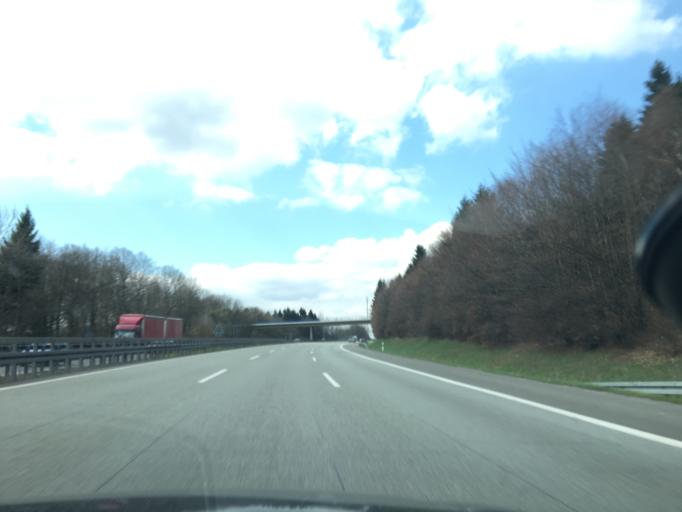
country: DE
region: North Rhine-Westphalia
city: Meinerzhagen
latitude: 51.1134
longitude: 7.6670
